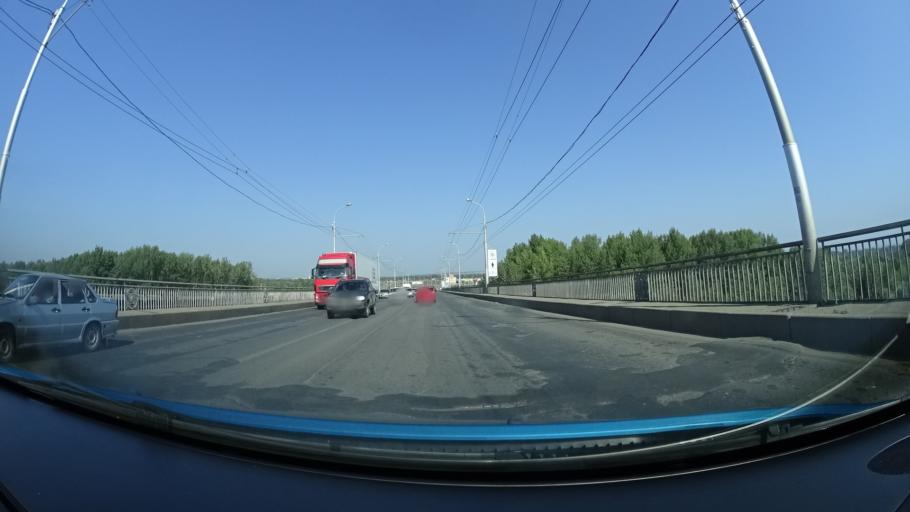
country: RU
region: Bashkortostan
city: Ufa
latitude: 54.7589
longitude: 55.9633
